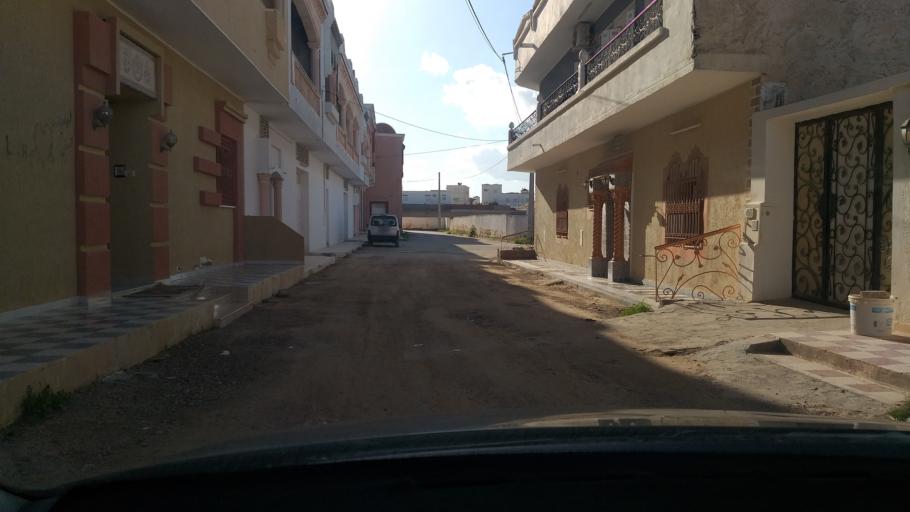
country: TN
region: Al Mahdiyah
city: El Jem
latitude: 35.2905
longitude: 10.7120
